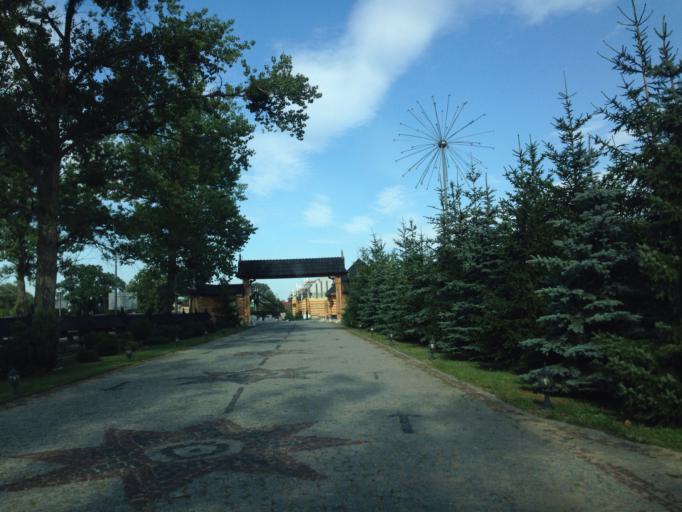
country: PL
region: Kujawsko-Pomorskie
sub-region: Powiat aleksandrowski
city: Ciechocinek
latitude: 52.8715
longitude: 18.7564
